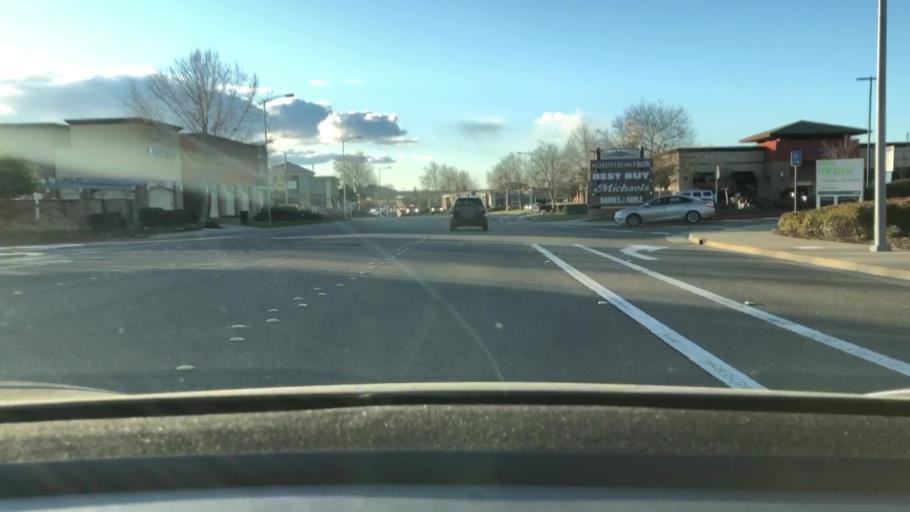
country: US
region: California
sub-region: Placer County
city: Roseville
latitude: 38.7713
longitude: -121.2626
